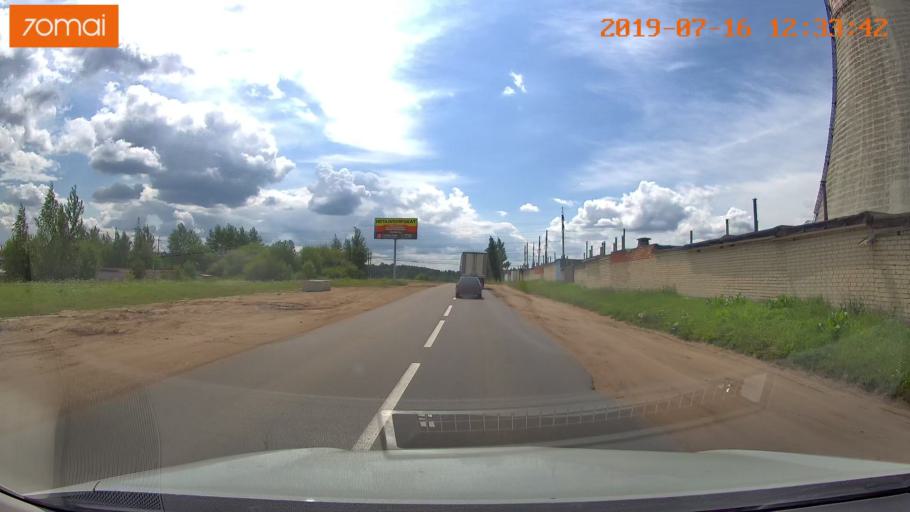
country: BY
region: Minsk
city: Malinovka
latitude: 53.8712
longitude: 27.4102
